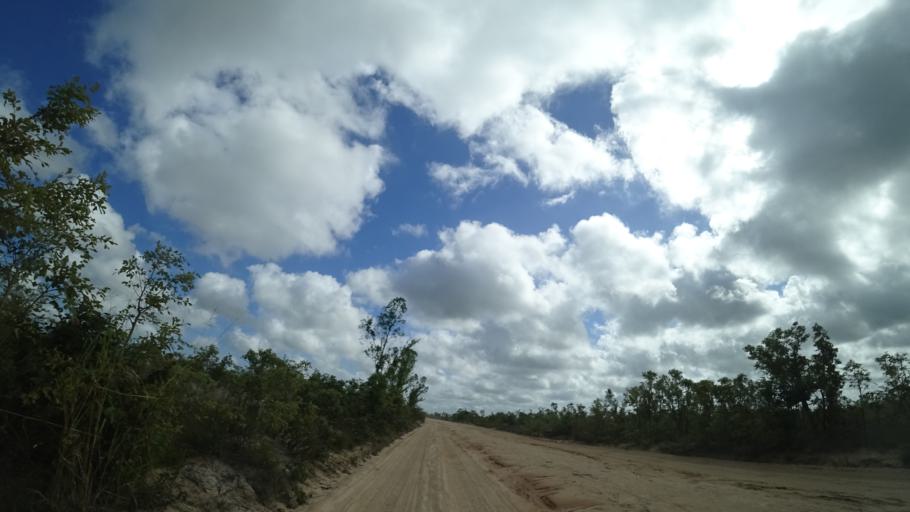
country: MZ
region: Sofala
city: Dondo
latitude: -19.4527
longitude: 34.7182
